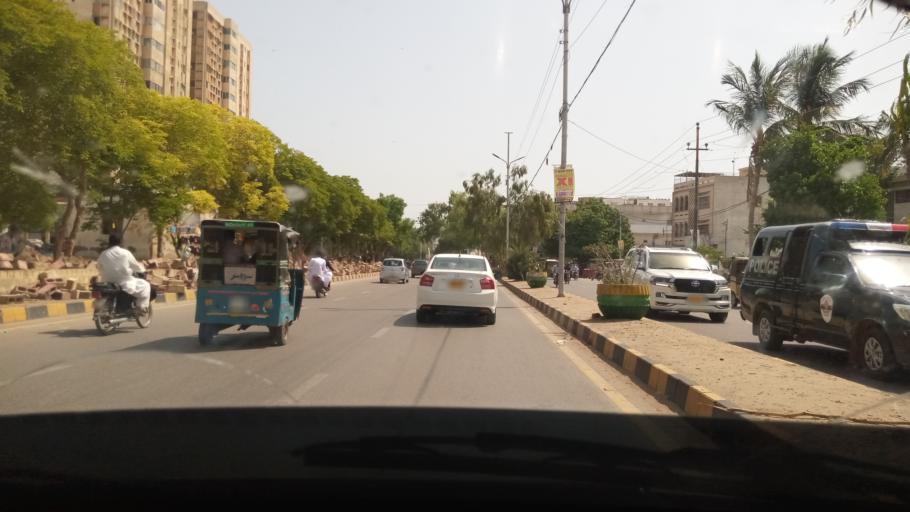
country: PK
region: Sindh
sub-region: Karachi District
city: Karachi
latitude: 24.8722
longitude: 67.0484
